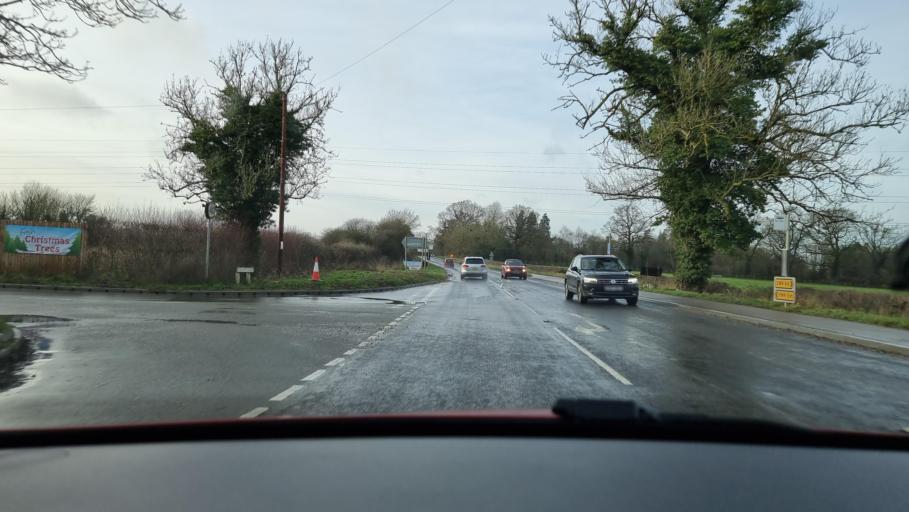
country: GB
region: England
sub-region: Buckinghamshire
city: Winslow
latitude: 51.9500
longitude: -0.8899
